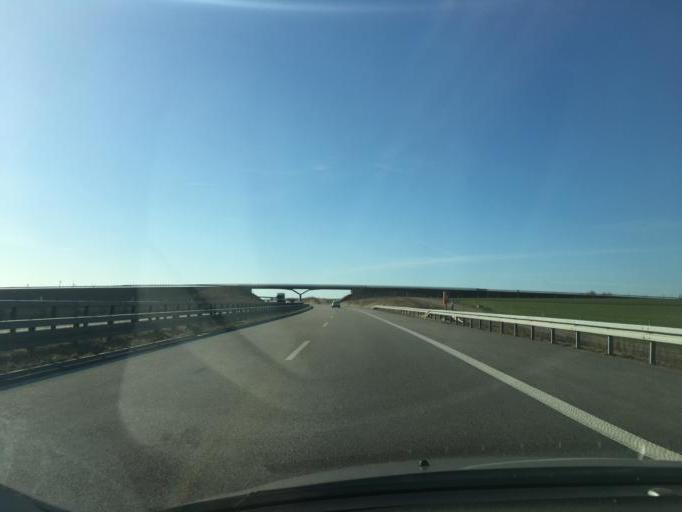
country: DE
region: Saxony
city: Narsdorf
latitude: 51.0103
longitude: 12.6834
